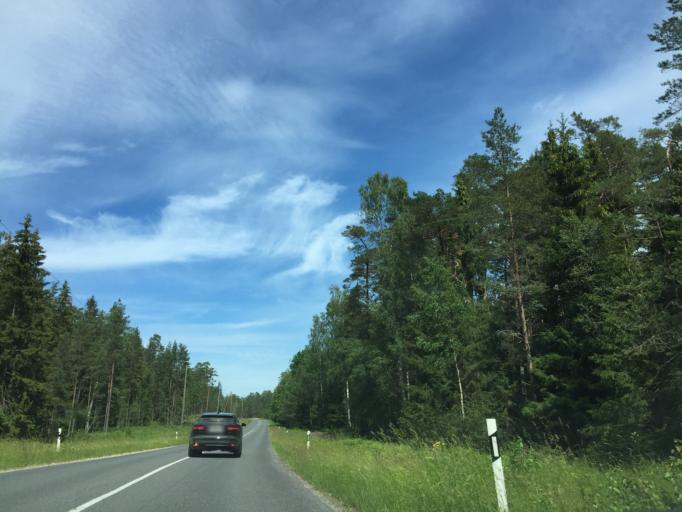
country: LV
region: Dundaga
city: Dundaga
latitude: 57.6401
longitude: 22.5672
